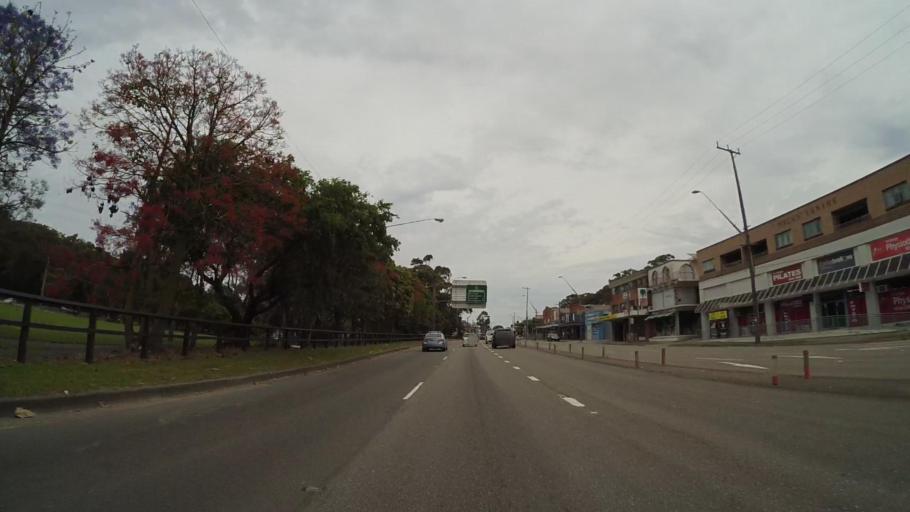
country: AU
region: New South Wales
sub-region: Kogarah
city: Blakehurst
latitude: -33.9887
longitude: 151.1124
